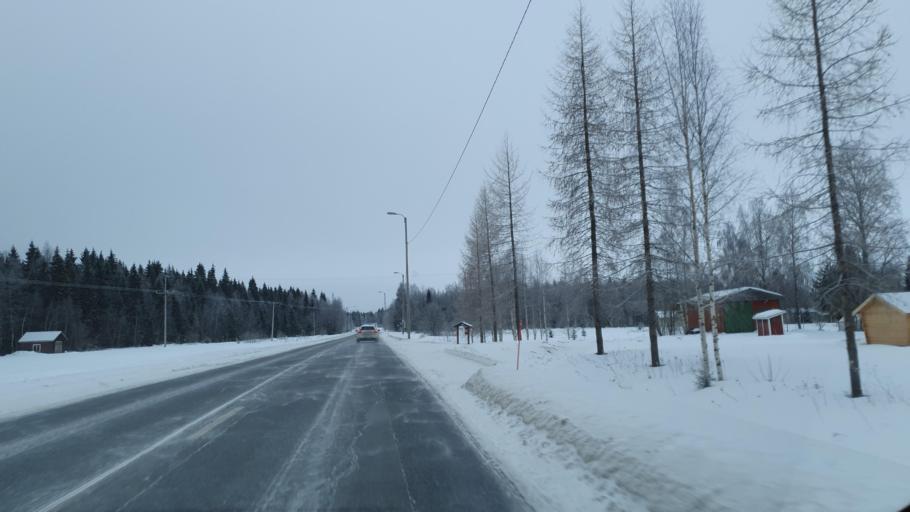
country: FI
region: Lapland
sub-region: Torniolaakso
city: Ylitornio
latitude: 66.1596
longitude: 23.9299
